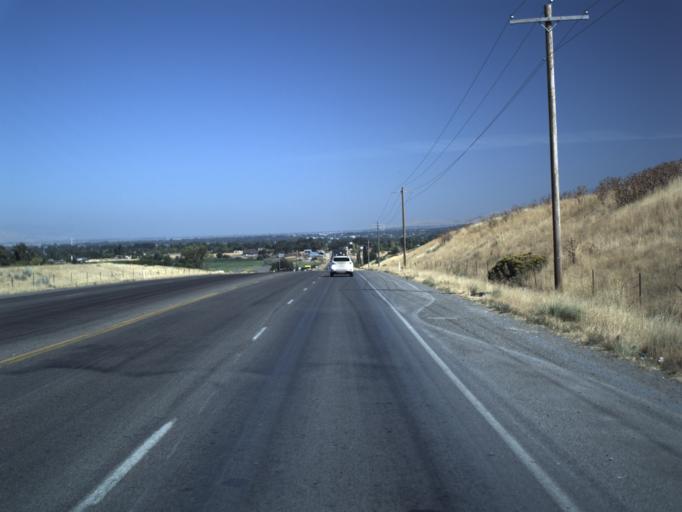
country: US
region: Utah
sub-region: Cache County
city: Hyrum
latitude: 41.6430
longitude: -111.8326
